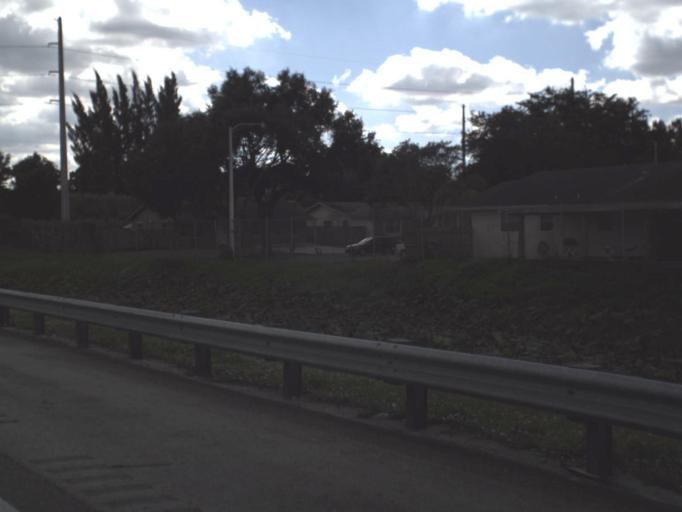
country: US
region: Florida
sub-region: Broward County
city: Pembroke Pines
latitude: 26.0334
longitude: -80.2136
